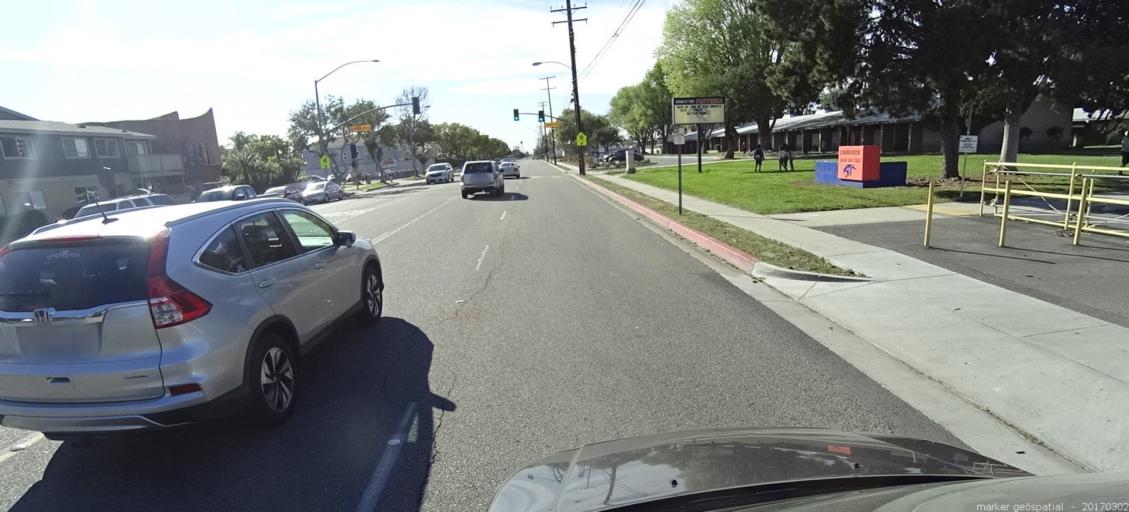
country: US
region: California
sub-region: Orange County
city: Cypress
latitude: 33.8246
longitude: -118.0125
